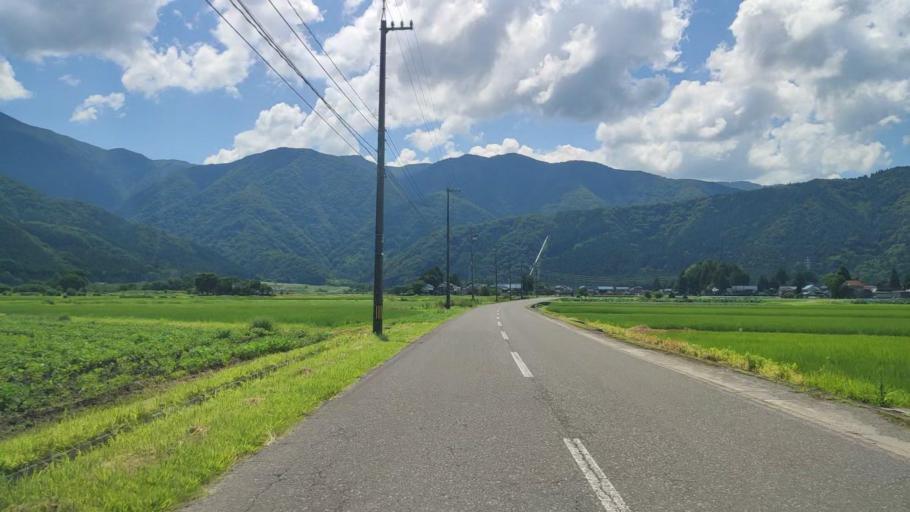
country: JP
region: Fukui
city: Ono
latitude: 35.9471
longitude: 136.5427
